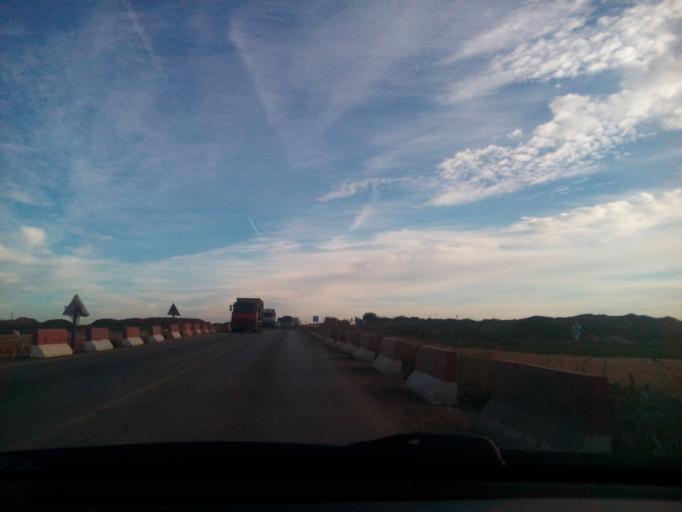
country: DZ
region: Relizane
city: Relizane
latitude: 35.7354
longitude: 0.3050
